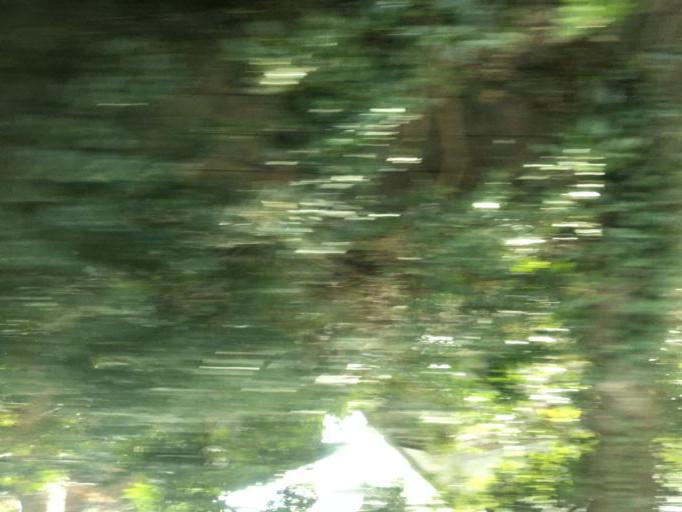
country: JP
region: Chiba
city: Narita
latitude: 35.7882
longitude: 140.3020
